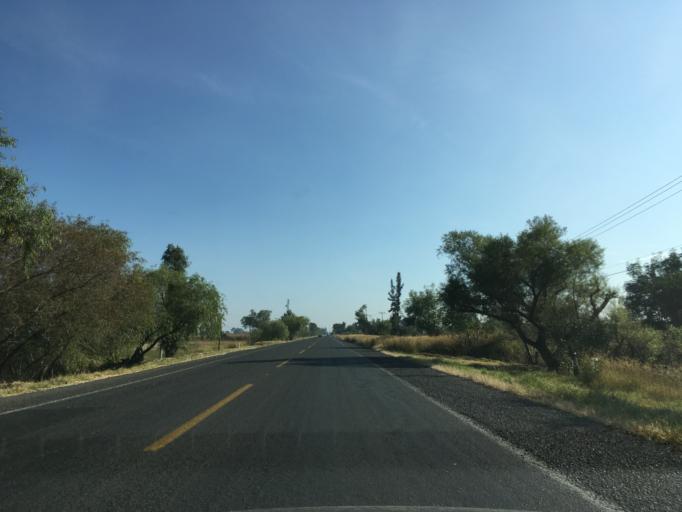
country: MX
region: Michoacan
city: Alvaro Obregon
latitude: 19.8315
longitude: -101.0351
